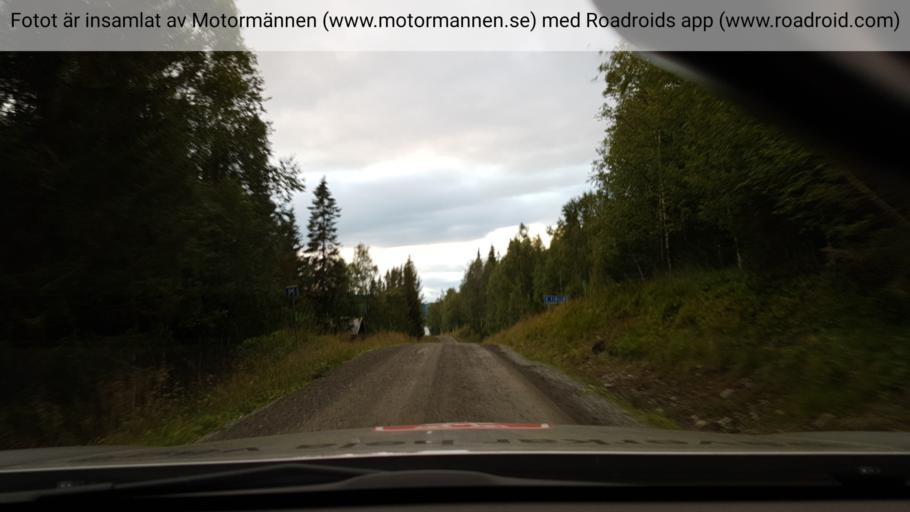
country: NO
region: Nordland
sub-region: Hattfjelldal
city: Hattfjelldal
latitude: 65.6200
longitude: 15.2428
